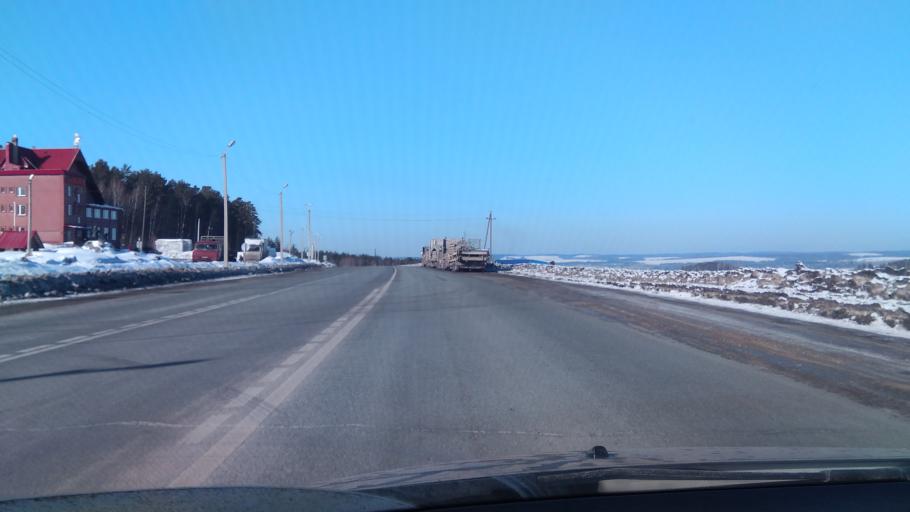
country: RU
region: Sverdlovsk
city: Bisert'
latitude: 56.8332
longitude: 58.8000
